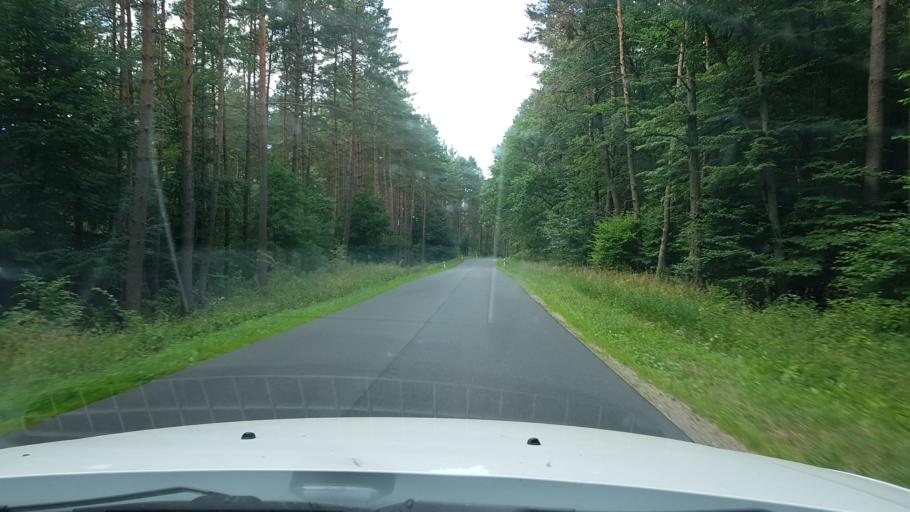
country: PL
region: West Pomeranian Voivodeship
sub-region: Powiat drawski
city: Zlocieniec
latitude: 53.5077
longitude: 16.0251
